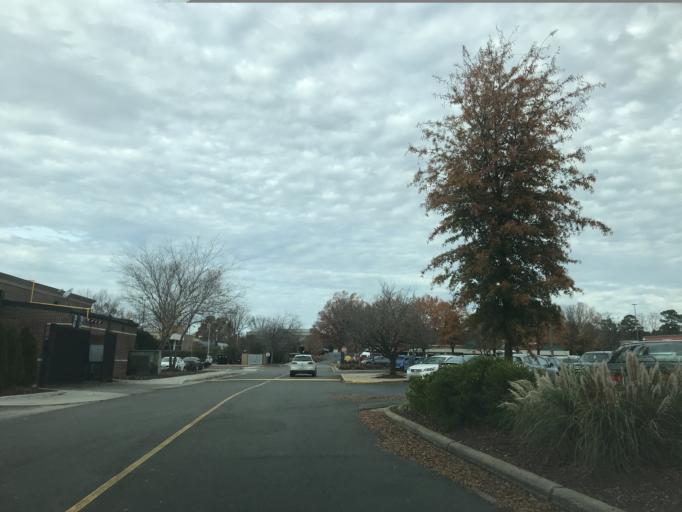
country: US
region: North Carolina
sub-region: Wake County
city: West Raleigh
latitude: 35.8652
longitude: -78.6195
